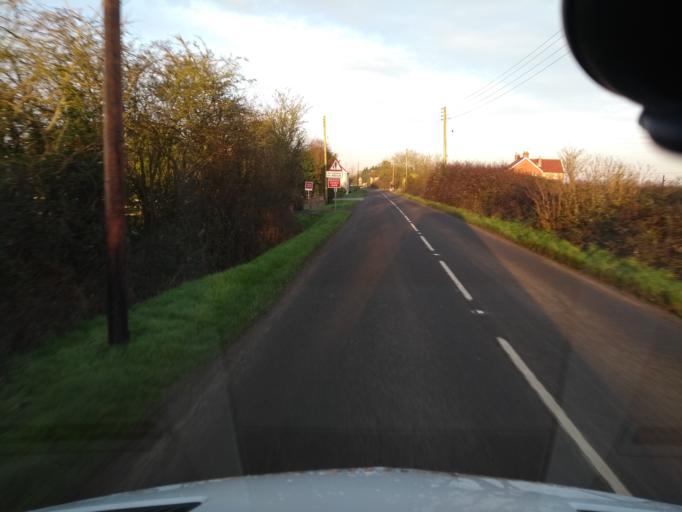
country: GB
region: England
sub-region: Somerset
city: Highbridge
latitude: 51.2179
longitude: -2.9450
